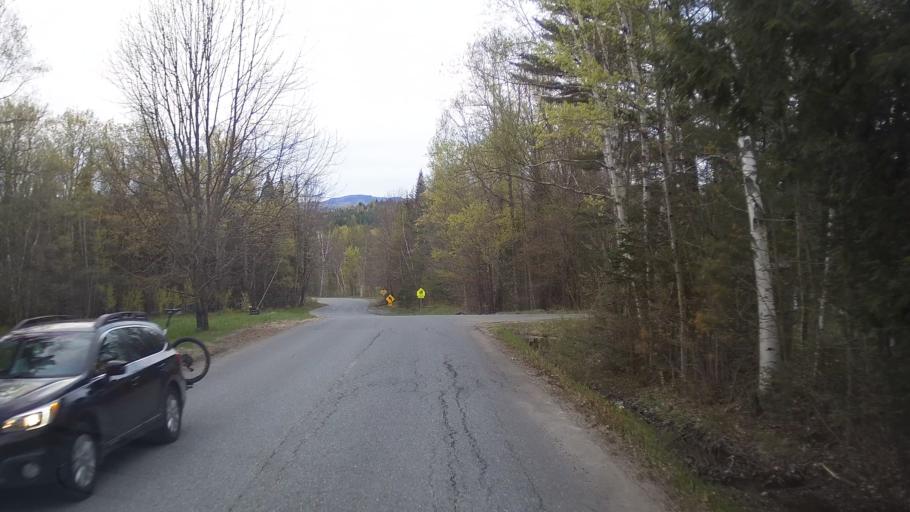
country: US
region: Vermont
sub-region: Caledonia County
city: Lyndonville
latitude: 44.5901
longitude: -71.9028
